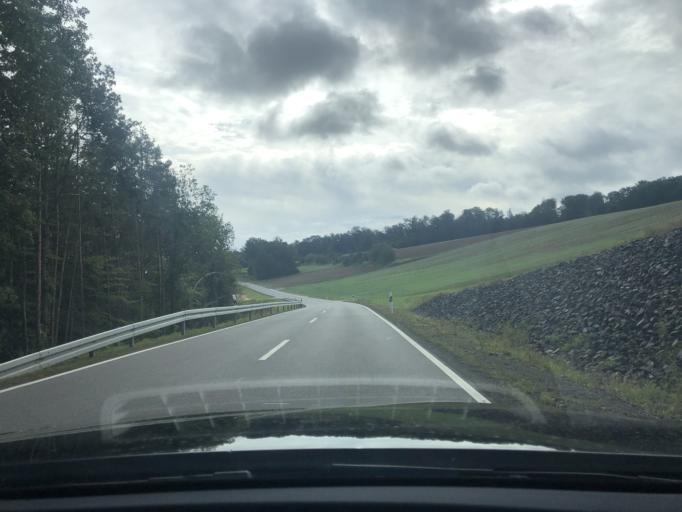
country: DE
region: Bavaria
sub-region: Regierungsbezirk Unterfranken
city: Rentweinsdorf
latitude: 50.0911
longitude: 10.8142
